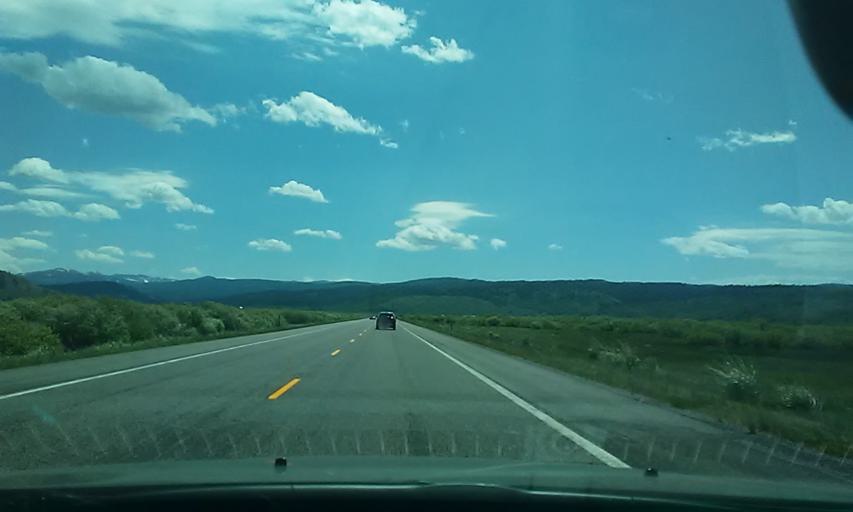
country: US
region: Wyoming
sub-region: Teton County
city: Jackson
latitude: 43.8368
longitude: -110.4350
